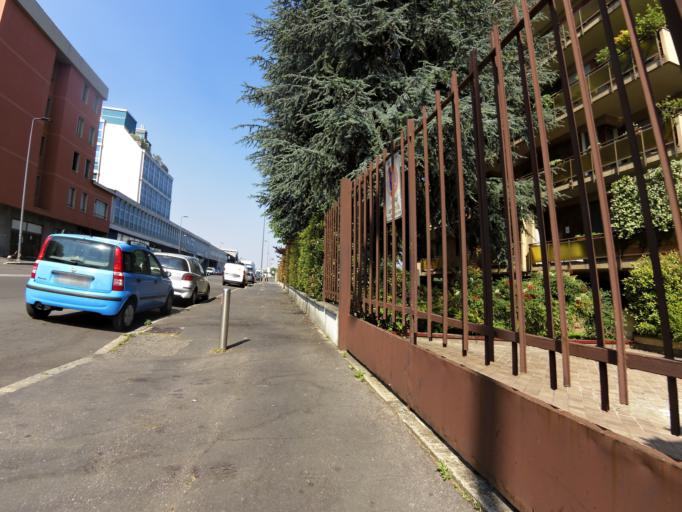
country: IT
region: Lombardy
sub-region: Citta metropolitana di Milano
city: Linate
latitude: 45.4511
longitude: 9.2511
